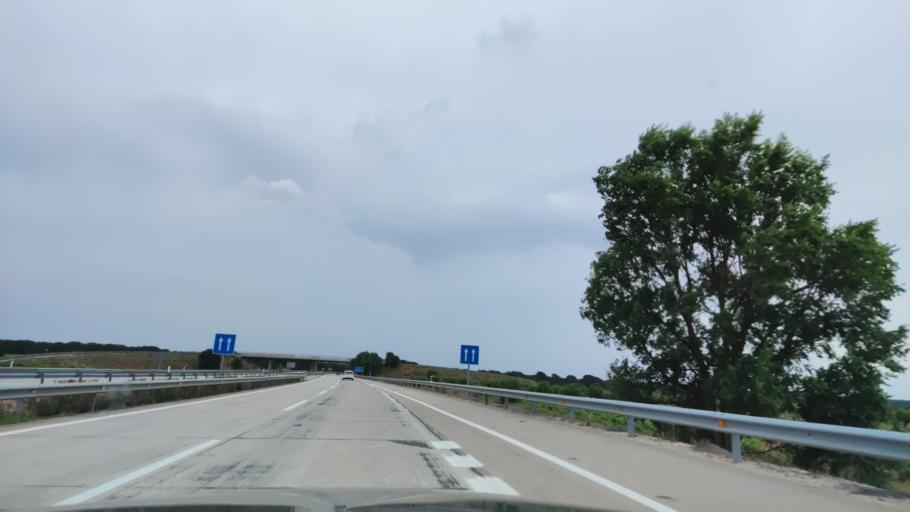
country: ES
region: Castille-La Mancha
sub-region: Provincia de Cuenca
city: Pozoamargo
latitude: 39.3535
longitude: -2.2034
